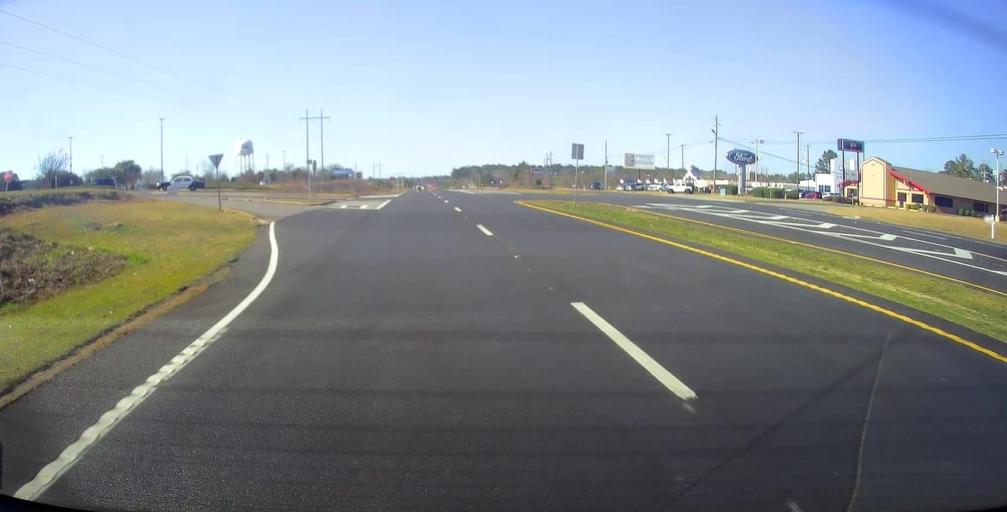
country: US
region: Georgia
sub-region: Sumter County
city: Americus
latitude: 32.0604
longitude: -84.1996
